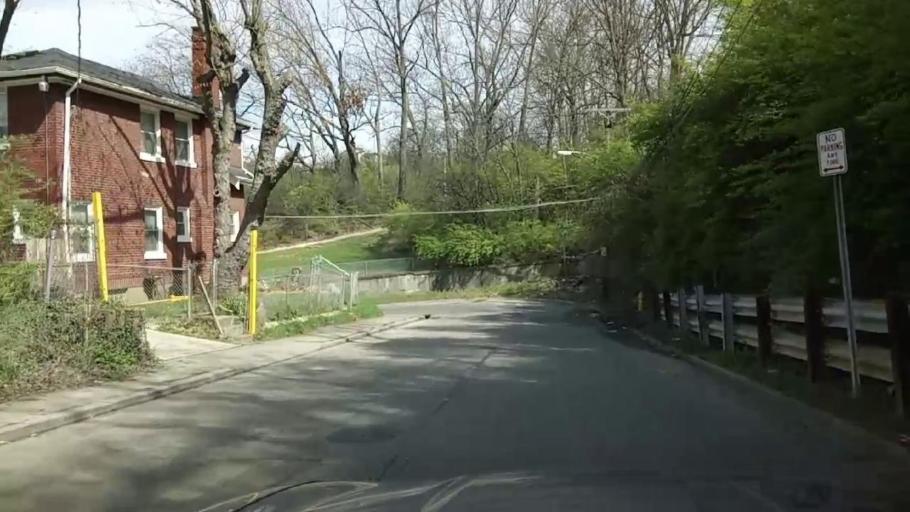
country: US
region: Kentucky
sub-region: Campbell County
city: Newport
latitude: 39.1230
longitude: -84.5132
